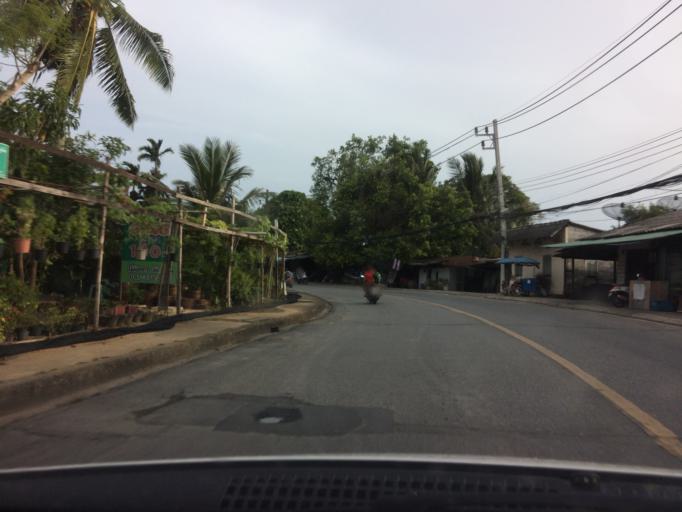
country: TH
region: Phuket
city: Ban Talat Yai
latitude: 7.8837
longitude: 98.4024
